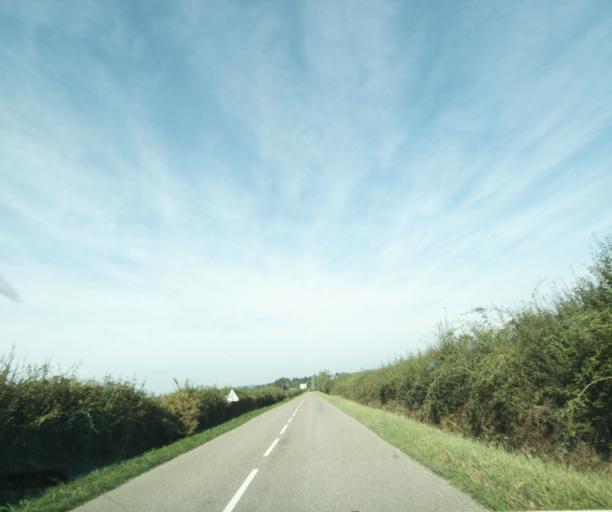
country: FR
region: Bourgogne
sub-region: Departement de Saone-et-Loire
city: Genelard
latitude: 46.5737
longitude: 4.2588
